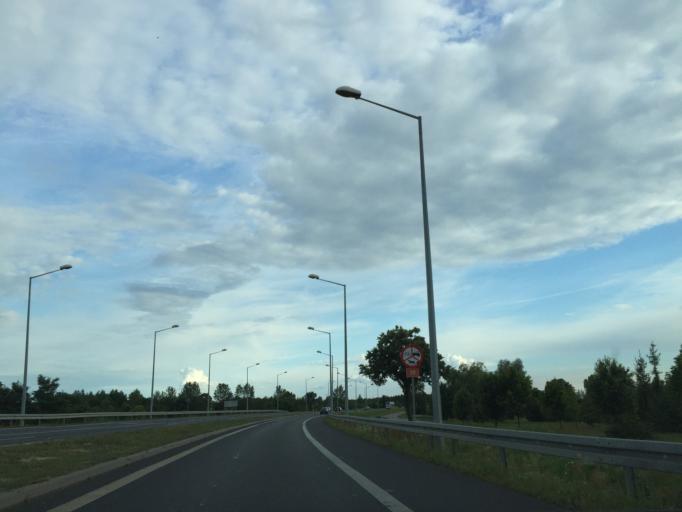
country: PL
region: Lublin Voivodeship
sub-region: Powiat lubartowski
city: Lubartow
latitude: 51.4796
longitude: 22.5891
